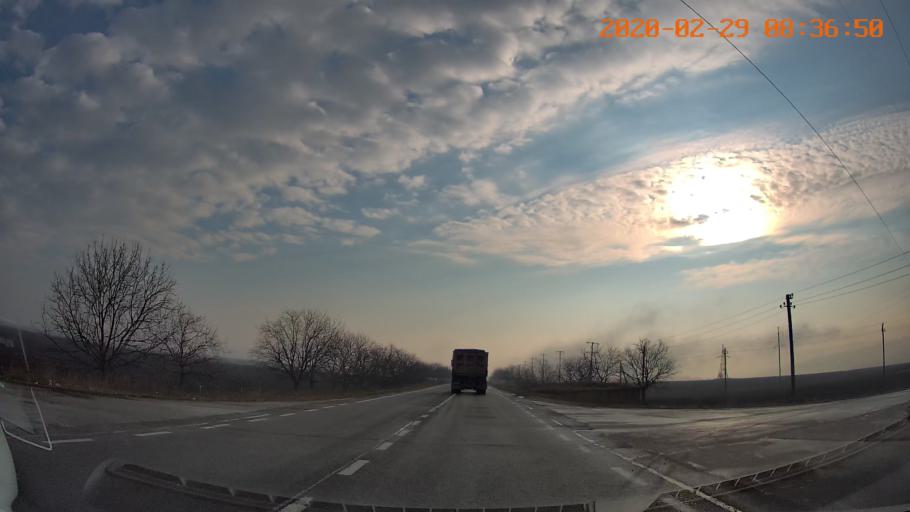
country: MD
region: Anenii Noi
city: Anenii Noi
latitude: 46.9215
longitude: 29.3522
